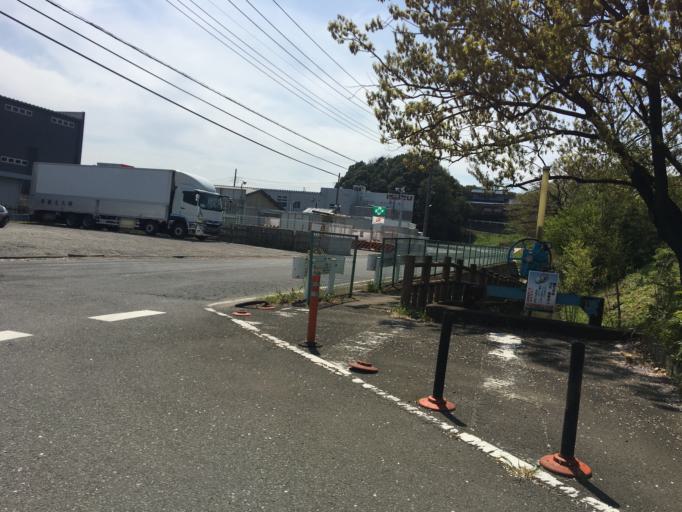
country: JP
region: Saitama
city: Shiki
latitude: 35.8261
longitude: 139.5515
